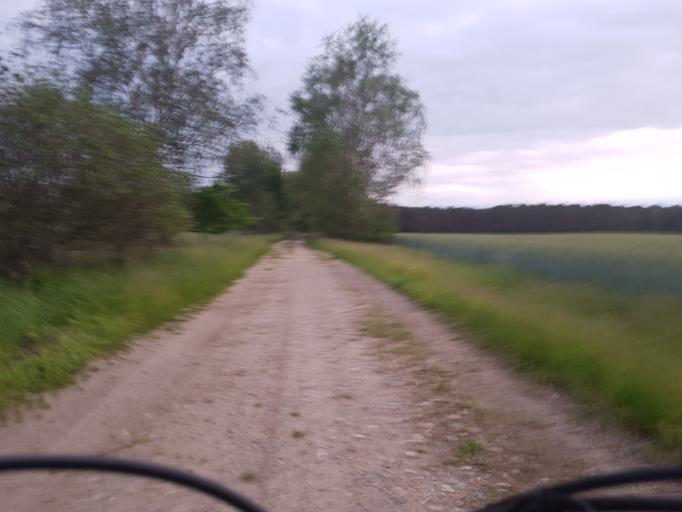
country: DE
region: Brandenburg
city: Schilda
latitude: 51.5655
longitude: 13.3866
